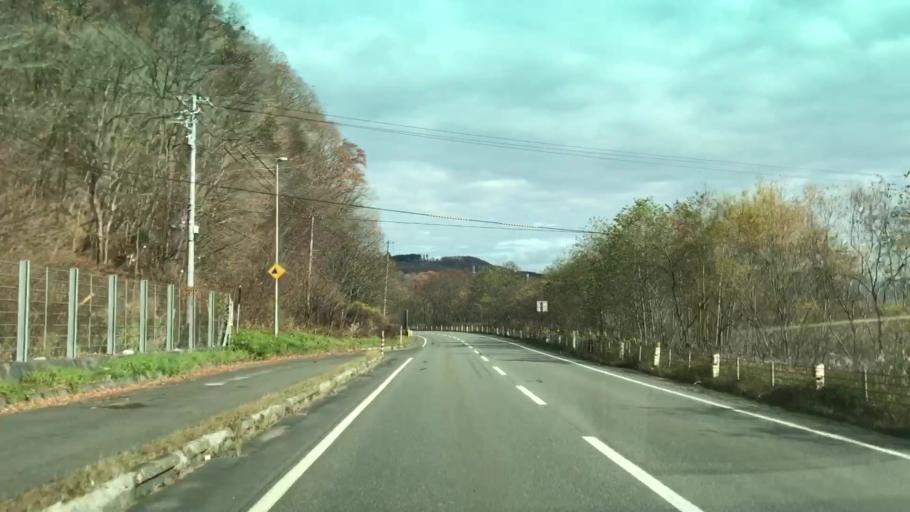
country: JP
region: Hokkaido
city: Shizunai-furukawacho
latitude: 42.7124
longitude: 142.2466
